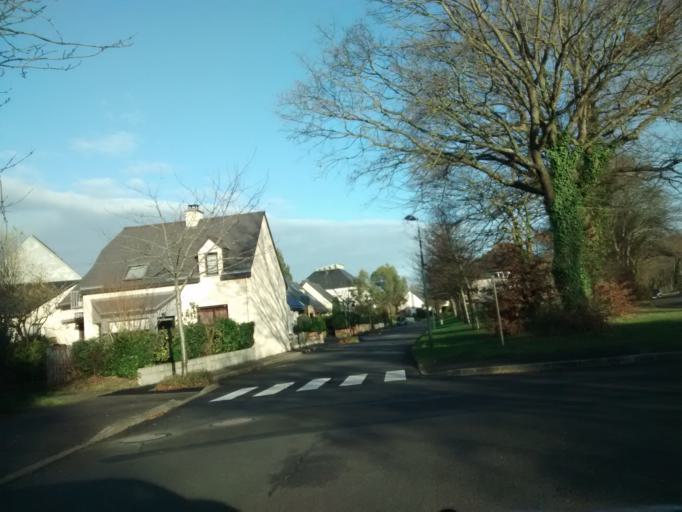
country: FR
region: Brittany
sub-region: Departement d'Ille-et-Vilaine
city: Chantepie
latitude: 48.0931
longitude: -1.6148
